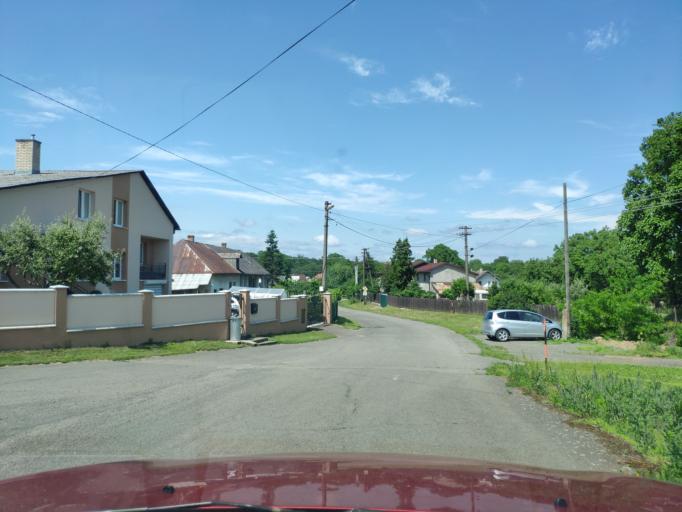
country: SK
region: Presovsky
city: Vranov nad Topl'ou
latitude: 48.8230
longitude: 21.6370
